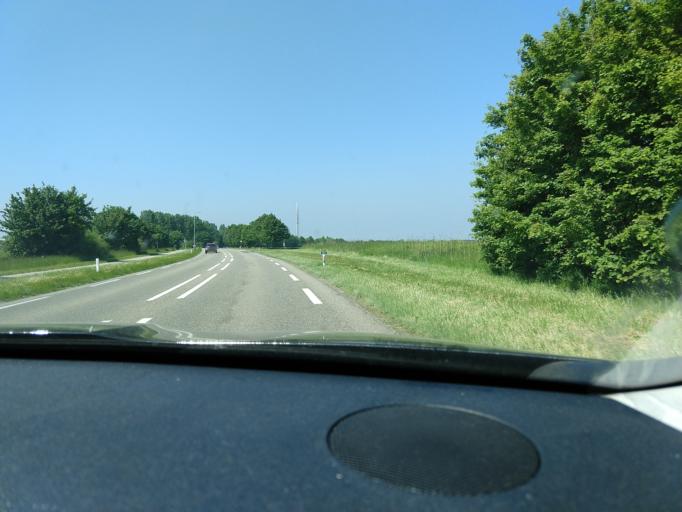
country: NL
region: Zeeland
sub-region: Gemeente Reimerswaal
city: Yerseke
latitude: 51.5497
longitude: 4.0987
